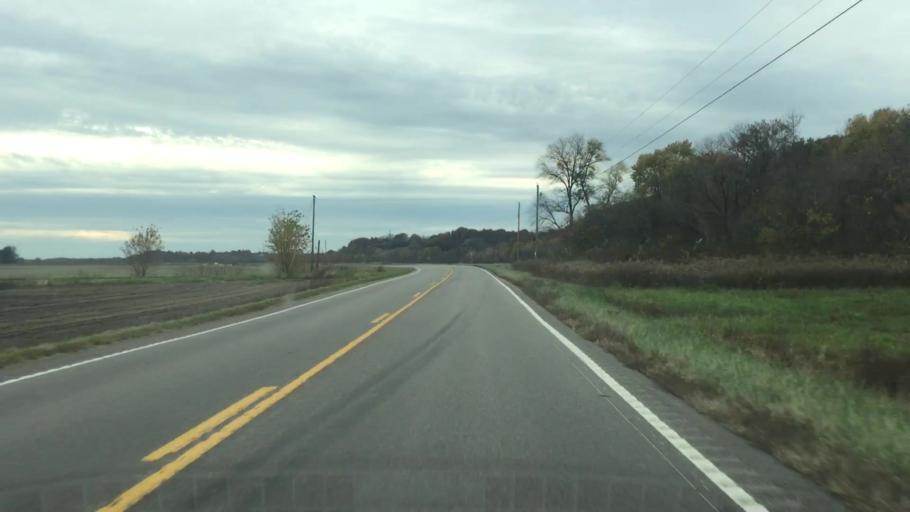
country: US
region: Missouri
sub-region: Callaway County
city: Fulton
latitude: 38.7073
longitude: -91.7915
